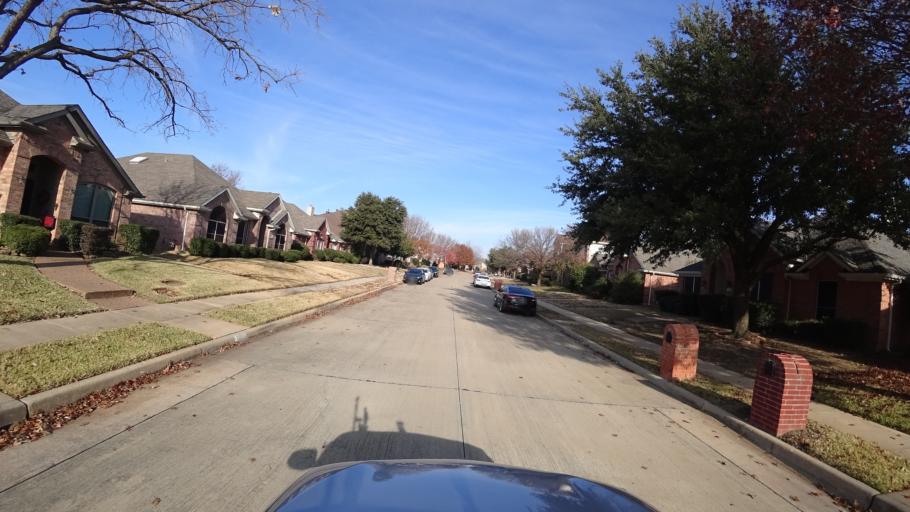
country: US
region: Texas
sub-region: Denton County
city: Lewisville
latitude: 33.0594
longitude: -97.0208
